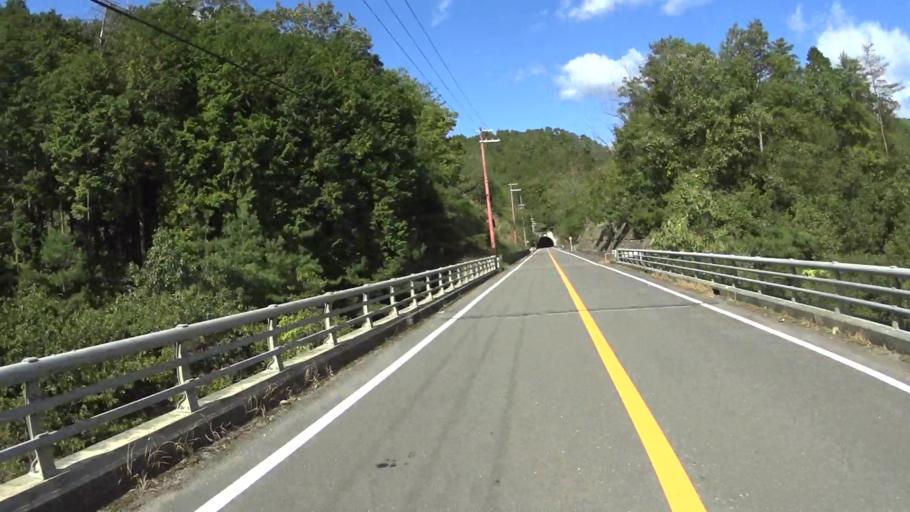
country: JP
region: Kyoto
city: Kameoka
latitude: 35.1349
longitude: 135.5352
